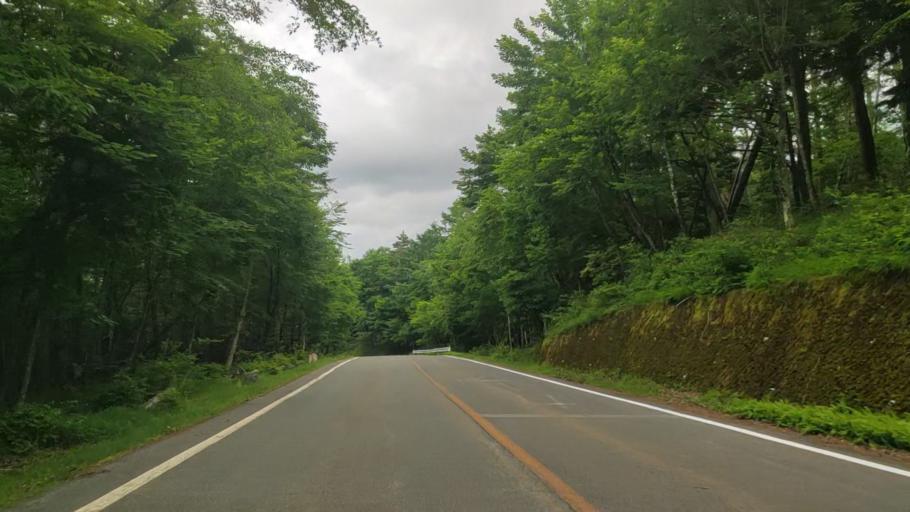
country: JP
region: Yamanashi
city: Fujikawaguchiko
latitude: 35.4259
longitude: 138.7358
